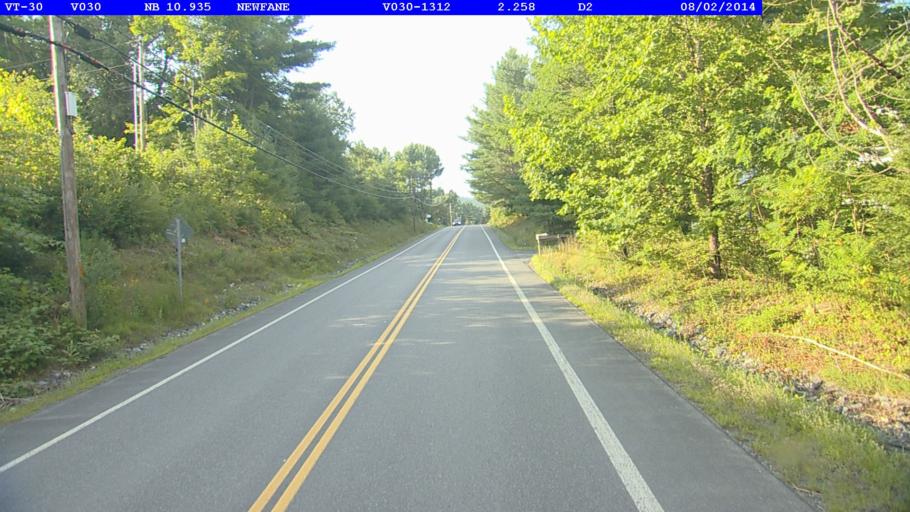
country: US
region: Vermont
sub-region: Windham County
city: Newfane
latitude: 42.9765
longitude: -72.6574
